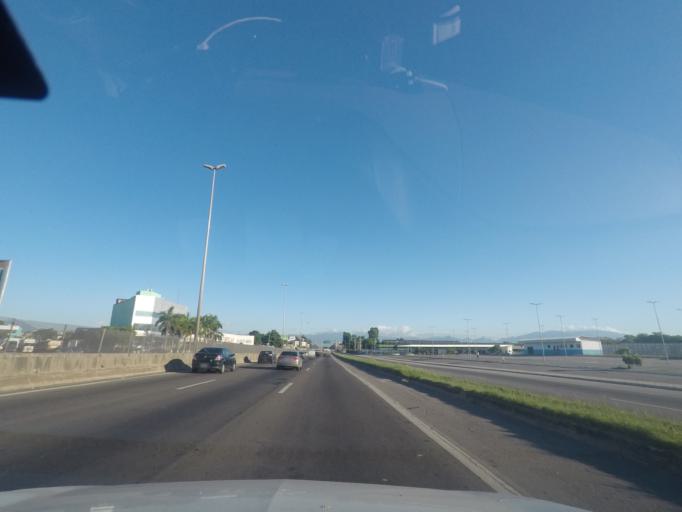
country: BR
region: Rio de Janeiro
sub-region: Duque De Caxias
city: Duque de Caxias
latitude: -22.7800
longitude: -43.2856
